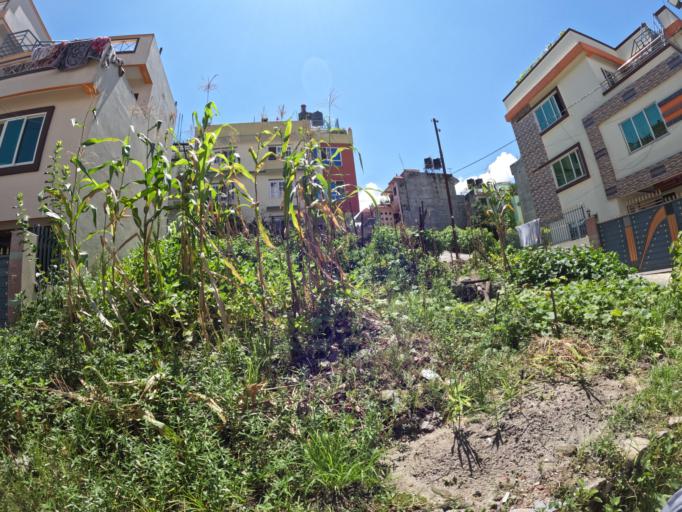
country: NP
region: Central Region
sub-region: Bagmati Zone
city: Kathmandu
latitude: 27.7503
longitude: 85.3303
